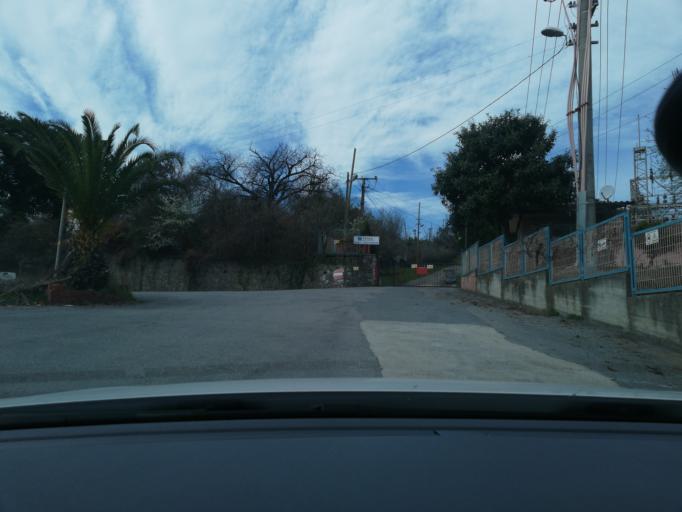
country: TR
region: Zonguldak
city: Eregli
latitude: 41.2916
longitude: 31.4044
